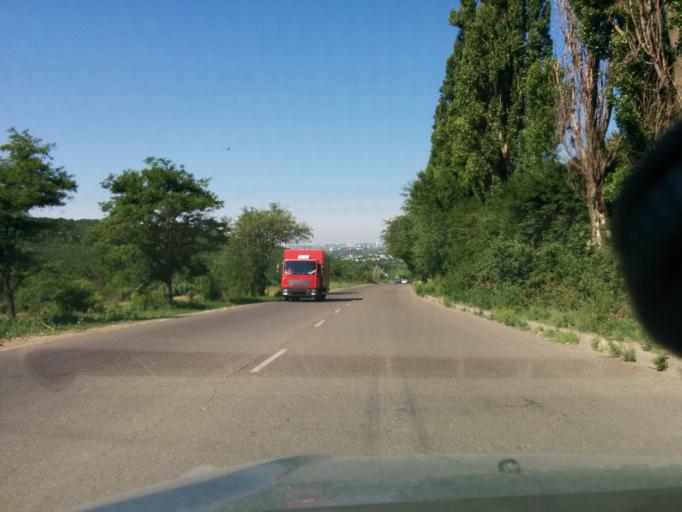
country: MD
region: Chisinau
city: Stauceni
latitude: 47.0509
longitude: 28.9336
